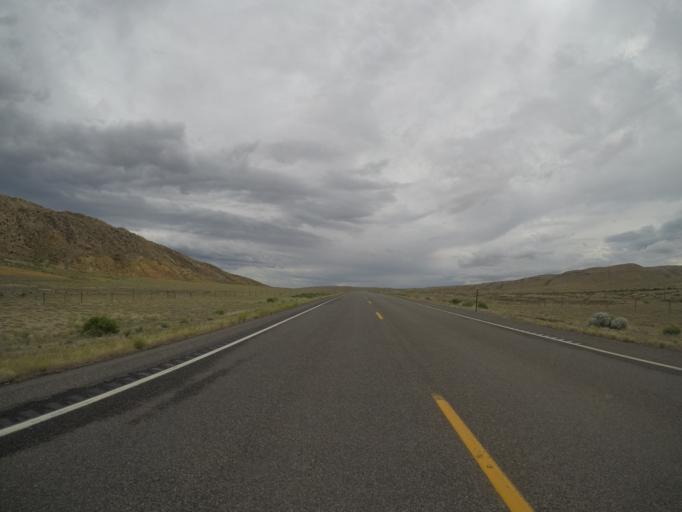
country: US
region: Wyoming
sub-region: Big Horn County
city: Lovell
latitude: 44.9437
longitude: -108.2966
